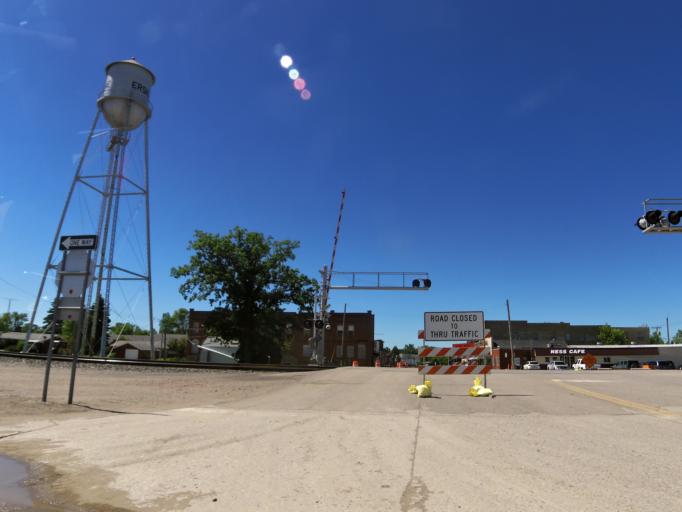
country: US
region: Minnesota
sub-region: Polk County
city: Fosston
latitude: 47.6688
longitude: -96.0092
